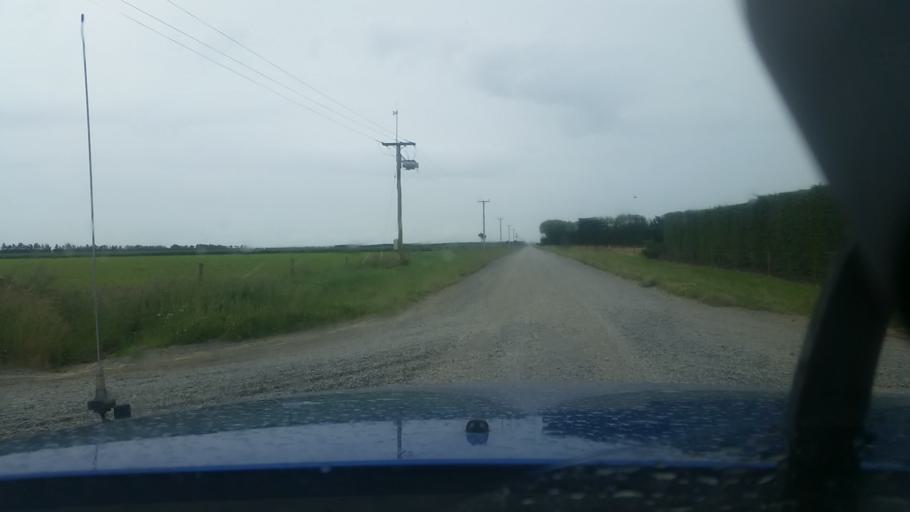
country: NZ
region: Canterbury
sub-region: Ashburton District
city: Rakaia
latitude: -43.9204
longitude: 172.1074
